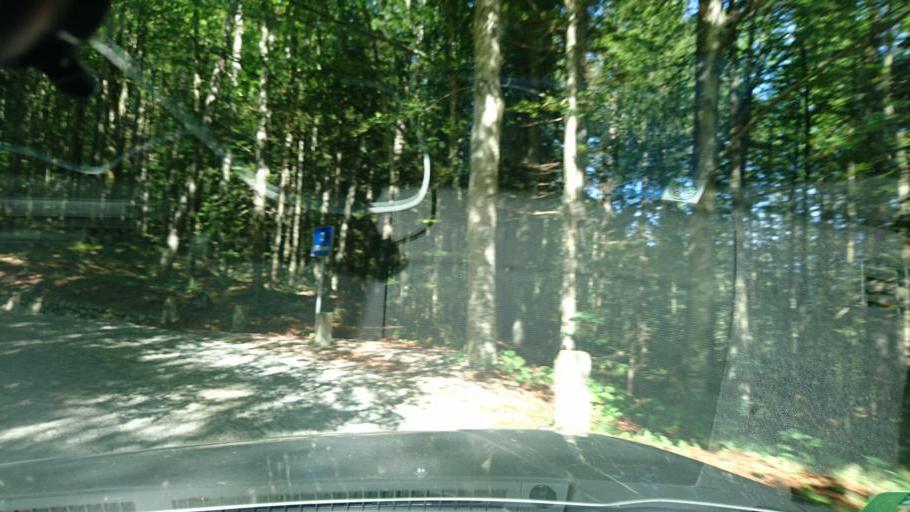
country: SI
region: Kranjska Gora
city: Kranjska Gora
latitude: 46.4619
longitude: 13.7808
